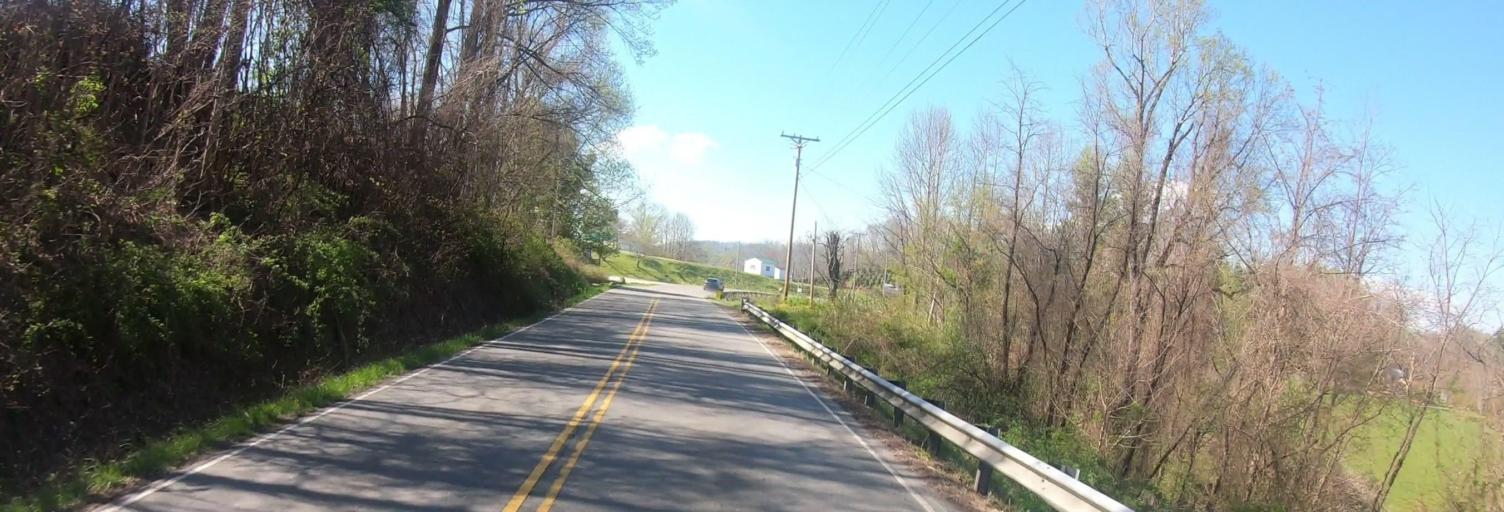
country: US
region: North Carolina
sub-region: Avery County
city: Newland
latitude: 35.9838
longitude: -81.9548
